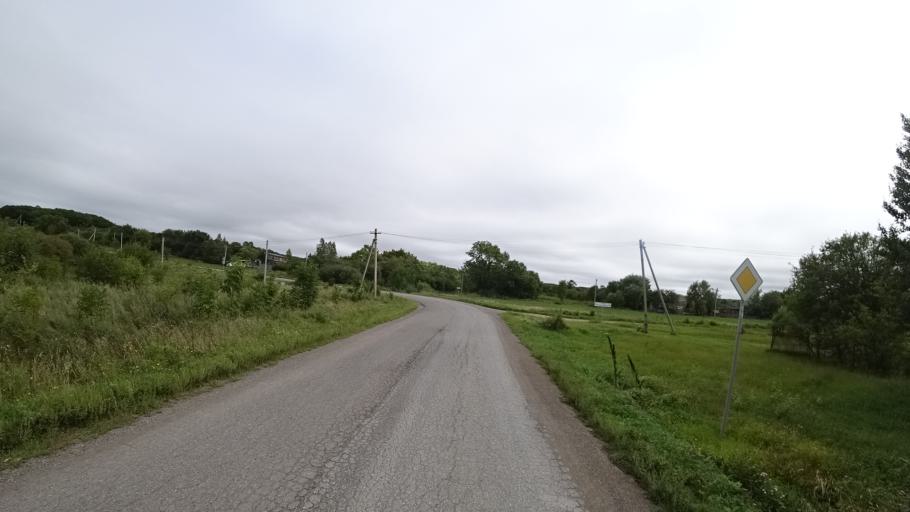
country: RU
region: Primorskiy
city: Lyalichi
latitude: 44.0735
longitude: 132.4638
